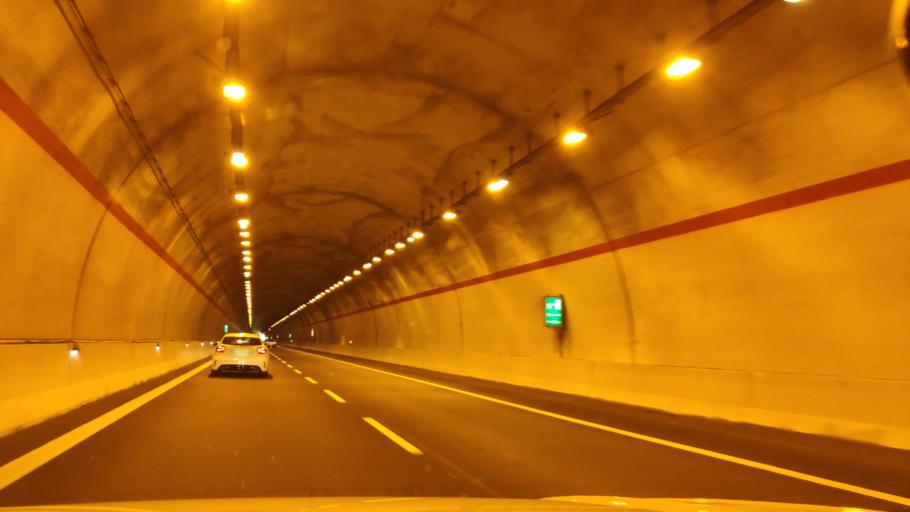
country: IT
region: Calabria
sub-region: Provincia di Cosenza
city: Mormanno
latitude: 39.9012
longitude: 15.9724
